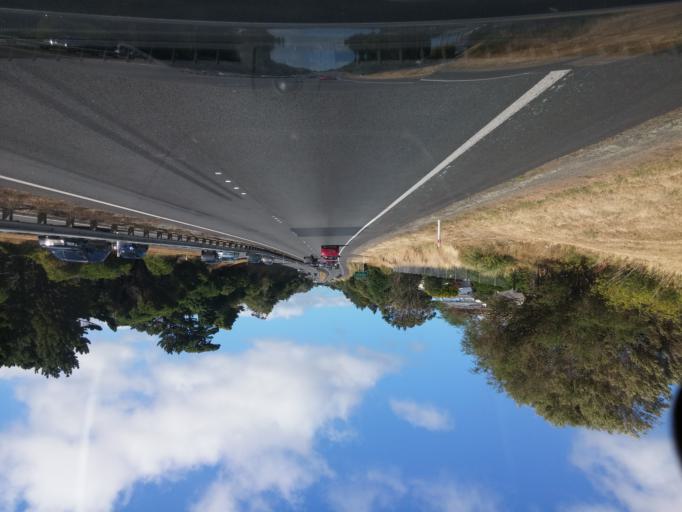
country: NZ
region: Wellington
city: Petone
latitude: -41.2090
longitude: 174.8165
